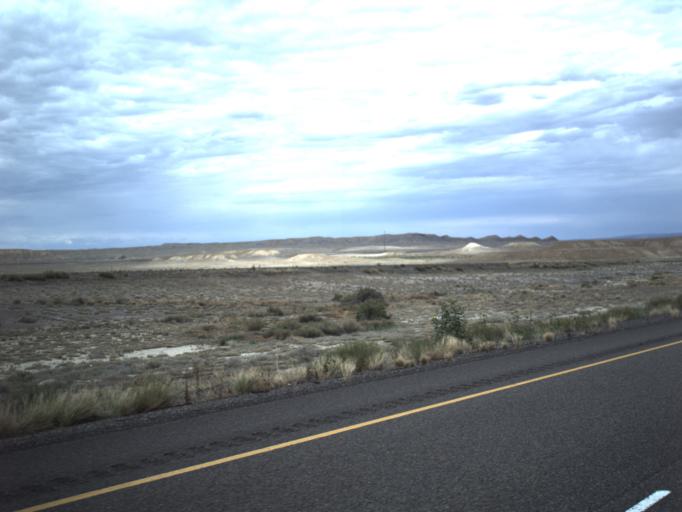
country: US
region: Utah
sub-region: Grand County
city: Moab
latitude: 38.9416
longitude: -109.5391
